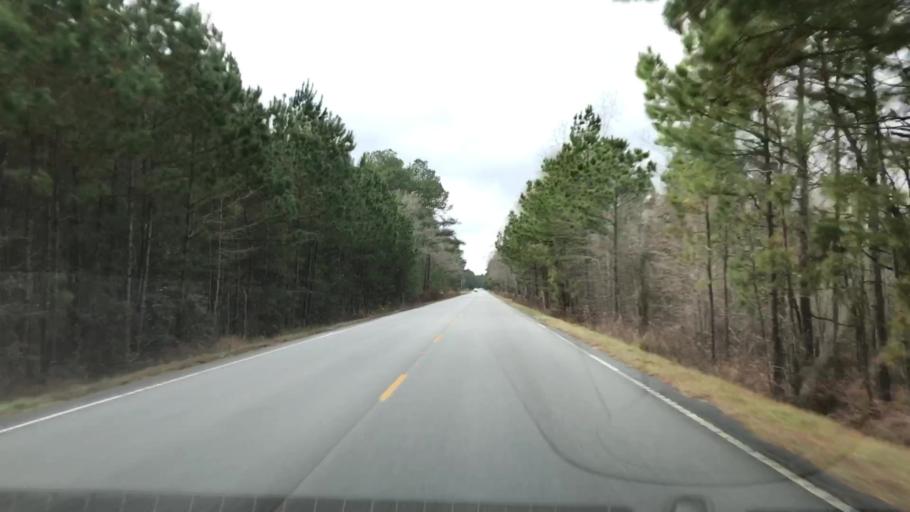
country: US
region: South Carolina
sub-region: Berkeley County
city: Saint Stephen
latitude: 33.2874
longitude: -79.7604
